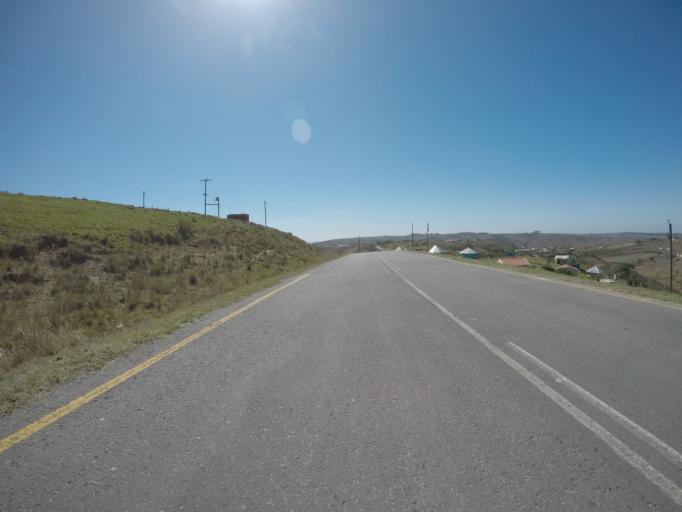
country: ZA
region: Eastern Cape
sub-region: OR Tambo District Municipality
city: Libode
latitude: -31.9130
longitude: 28.9837
